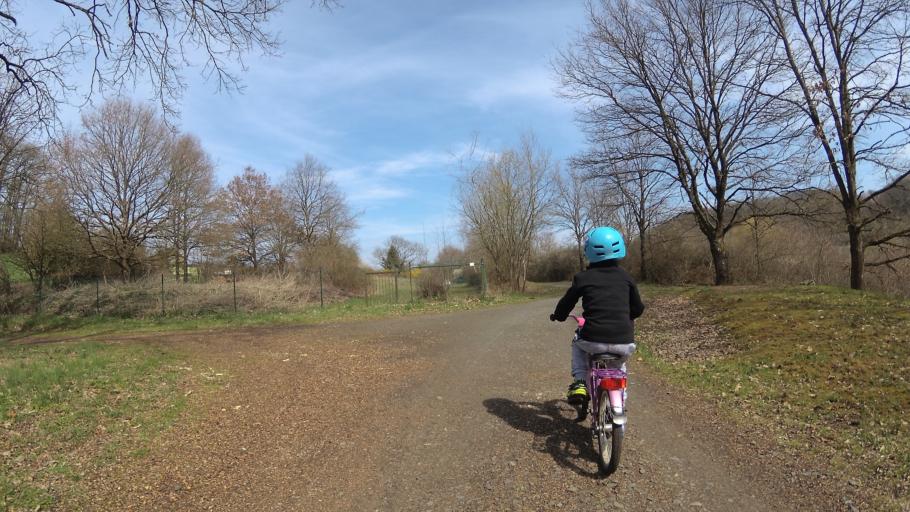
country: DE
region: Rheinland-Pfalz
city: Nanzdietschweiler
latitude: 49.4315
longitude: 7.4363
